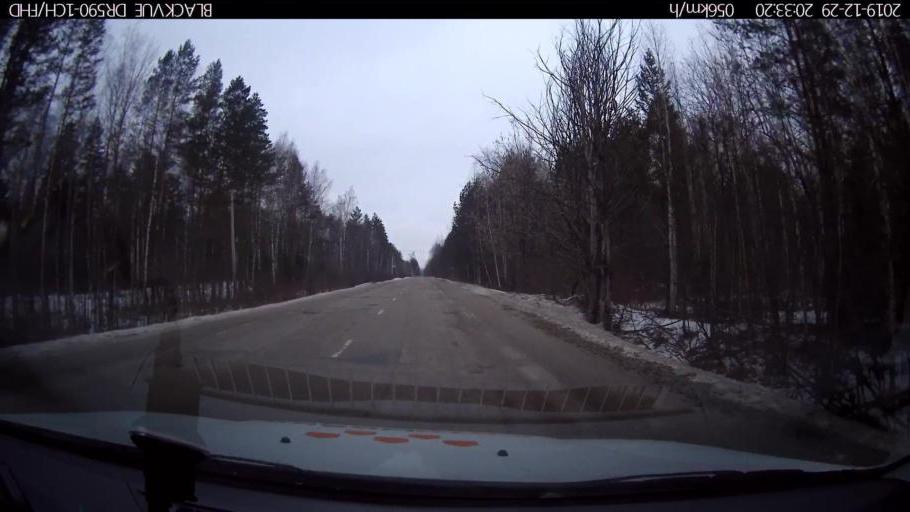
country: RU
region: Nizjnij Novgorod
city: Afonino
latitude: 56.1800
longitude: 44.0531
